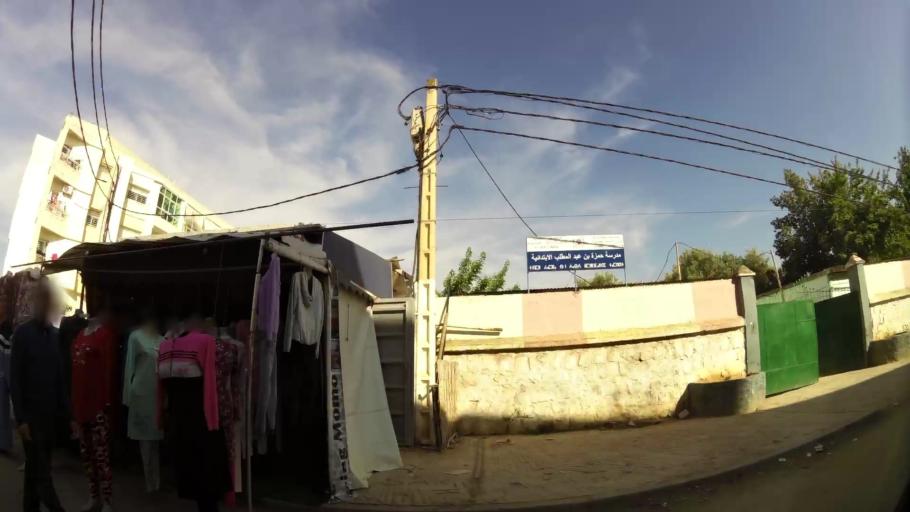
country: MA
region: Fes-Boulemane
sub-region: Fes
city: Fes
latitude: 34.0215
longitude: -5.0328
